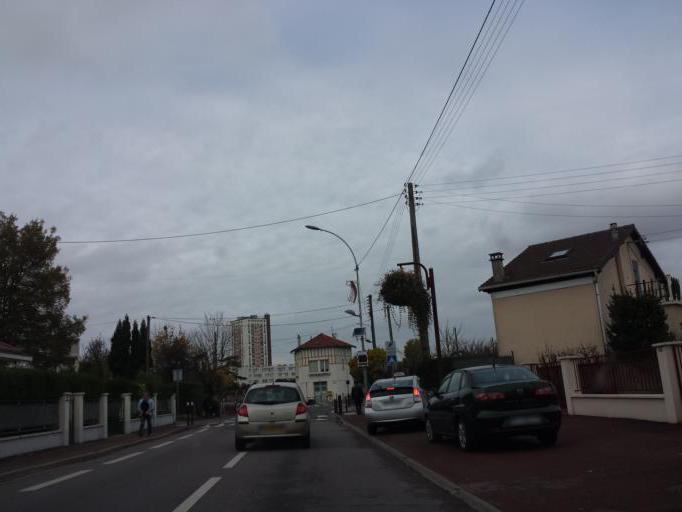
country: FR
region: Ile-de-France
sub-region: Departement du Val-d'Oise
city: Ermont
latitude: 48.9932
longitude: 2.2576
